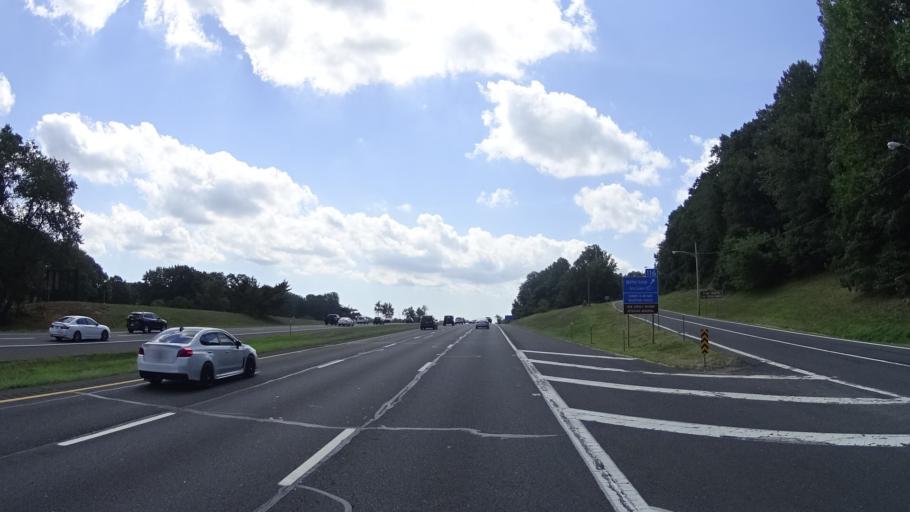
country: US
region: New Jersey
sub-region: Monmouth County
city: Strathmore
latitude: 40.3930
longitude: -74.1826
